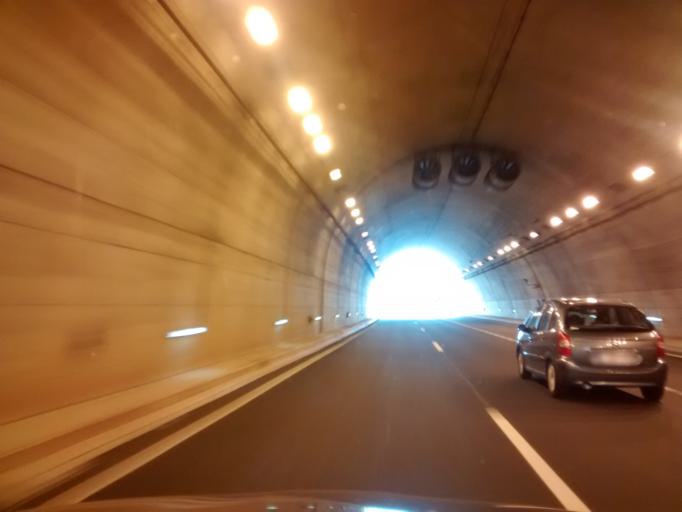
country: ES
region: Cantabria
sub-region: Provincia de Cantabria
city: Camargo
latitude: 43.4131
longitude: -3.8724
